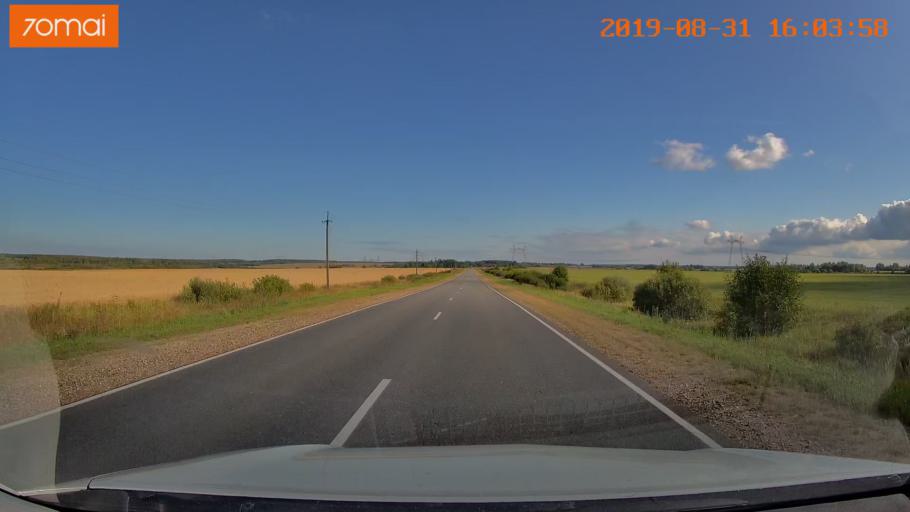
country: RU
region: Kaluga
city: Yukhnov
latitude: 54.6595
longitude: 35.3213
